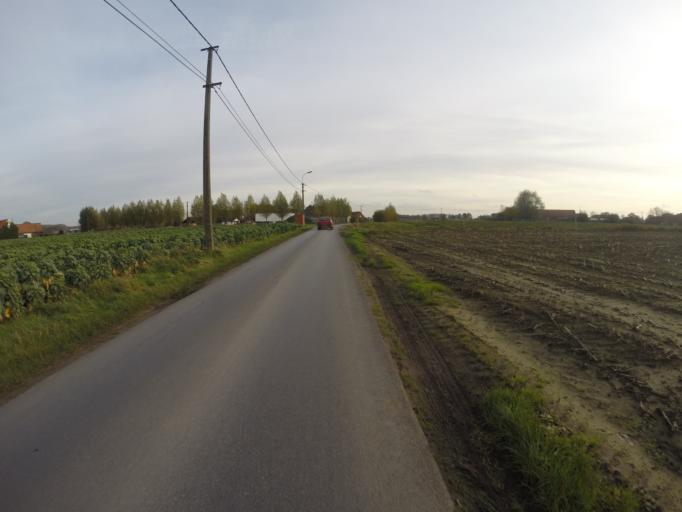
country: BE
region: Flanders
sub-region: Provincie Oost-Vlaanderen
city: Aalter
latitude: 51.0591
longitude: 3.4787
